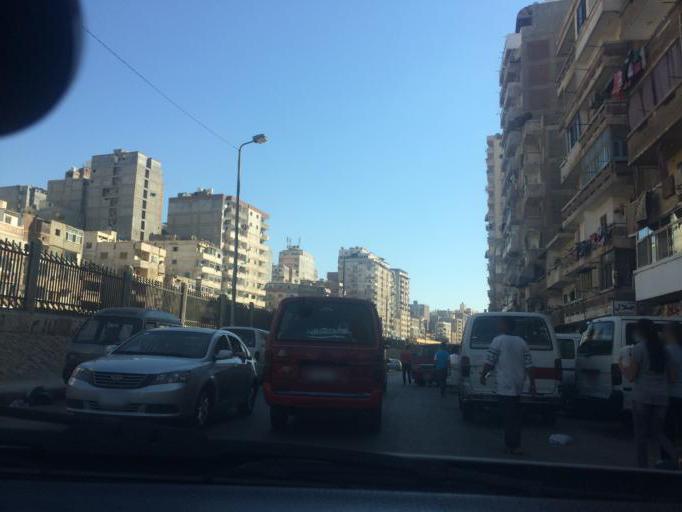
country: EG
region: Alexandria
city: Alexandria
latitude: 31.2595
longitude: 29.9964
